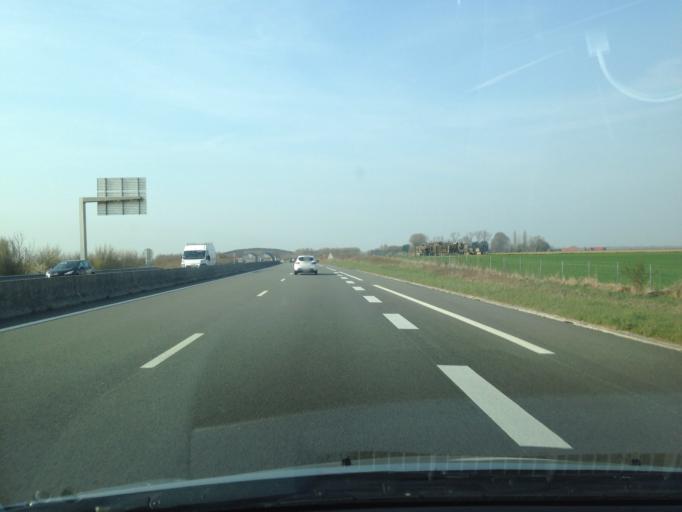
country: FR
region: Picardie
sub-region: Departement de la Somme
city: Nouvion
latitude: 50.2542
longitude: 1.7494
